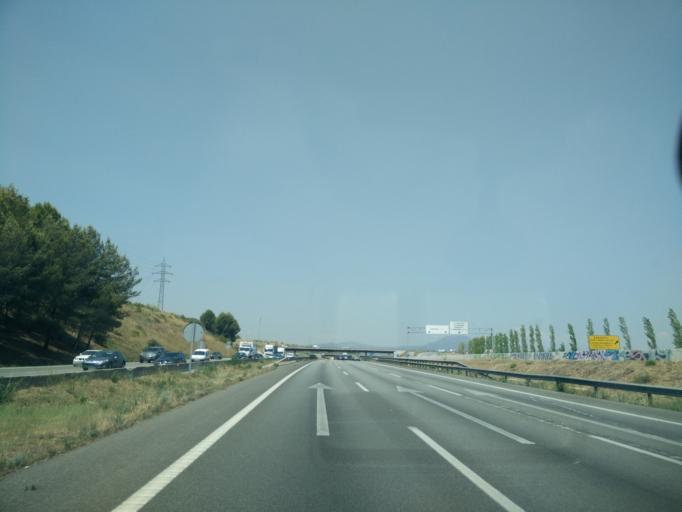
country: ES
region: Catalonia
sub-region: Provincia de Barcelona
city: Barbera del Valles
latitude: 41.5099
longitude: 2.1045
